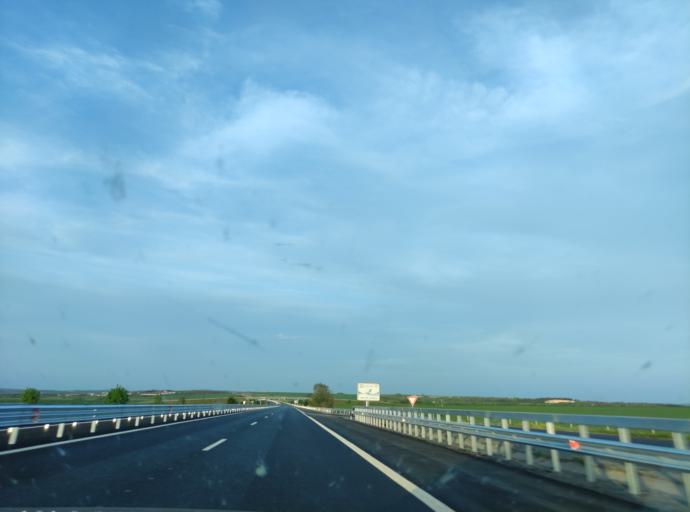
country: BG
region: Stara Zagora
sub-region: Obshtina Chirpan
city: Chirpan
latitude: 42.1956
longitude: 25.2507
